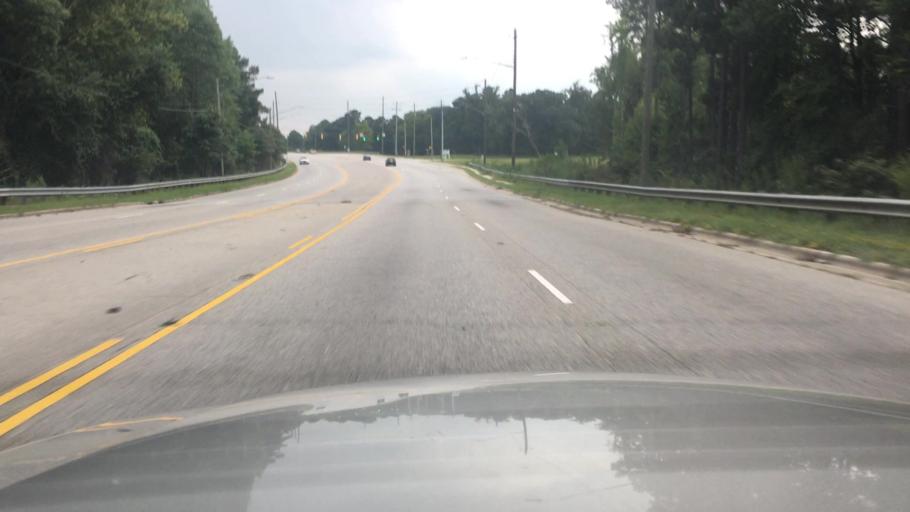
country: US
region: North Carolina
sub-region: Cumberland County
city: Fort Bragg
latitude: 35.1015
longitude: -78.9630
